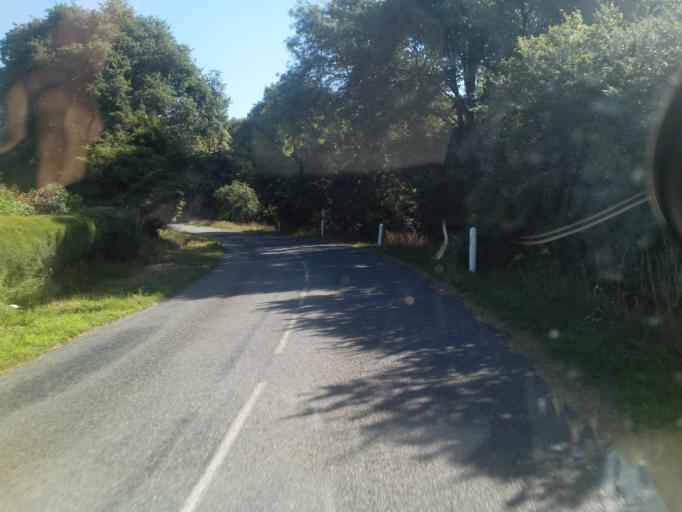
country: FR
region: Brittany
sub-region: Departement du Morbihan
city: Campeneac
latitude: 47.9809
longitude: -2.2696
